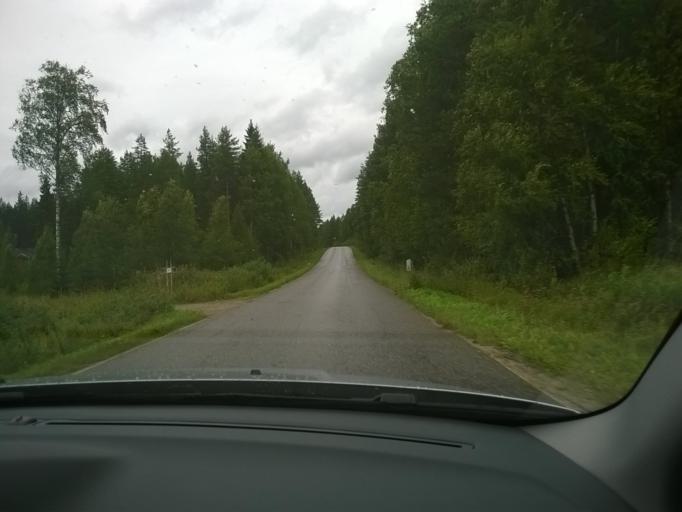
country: FI
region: Kainuu
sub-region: Kehys-Kainuu
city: Kuhmo
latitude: 64.1322
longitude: 29.4410
